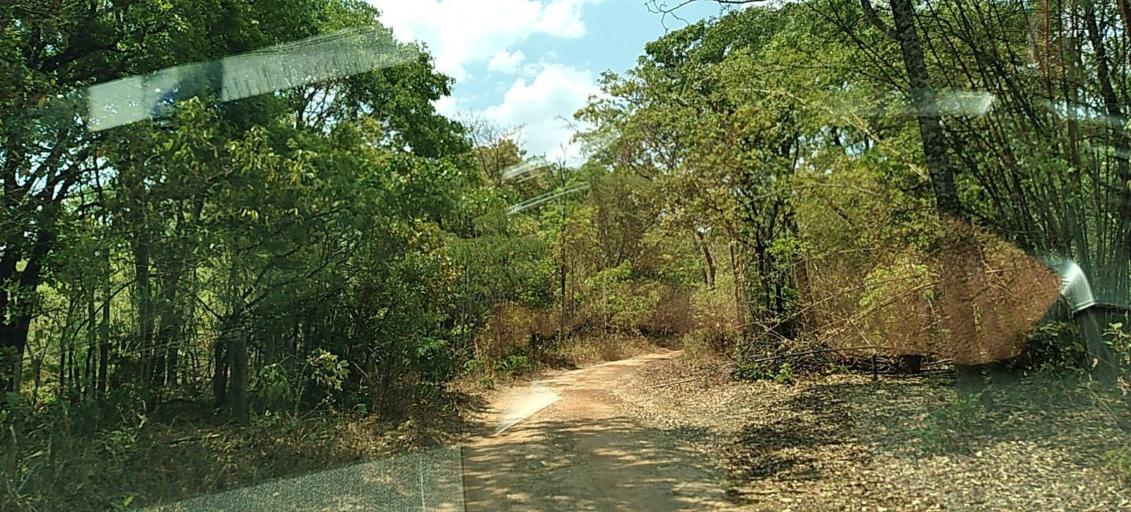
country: ZM
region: Copperbelt
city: Chililabombwe
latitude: -12.4814
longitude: 27.6436
